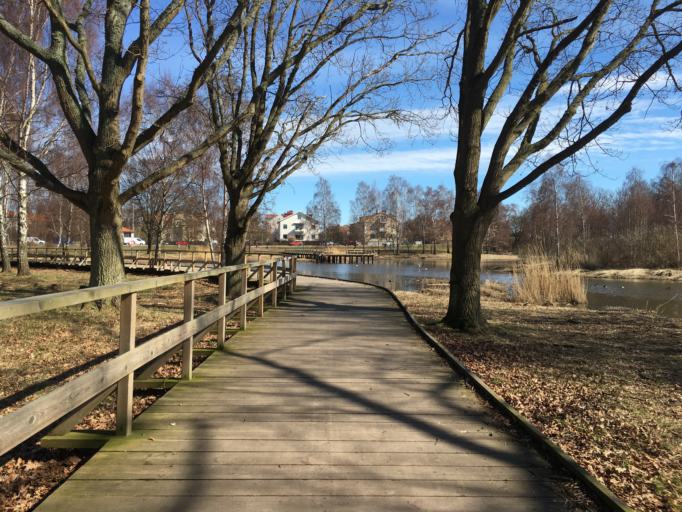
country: SE
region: Kalmar
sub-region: Kalmar Kommun
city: Kalmar
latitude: 56.6540
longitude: 16.3347
